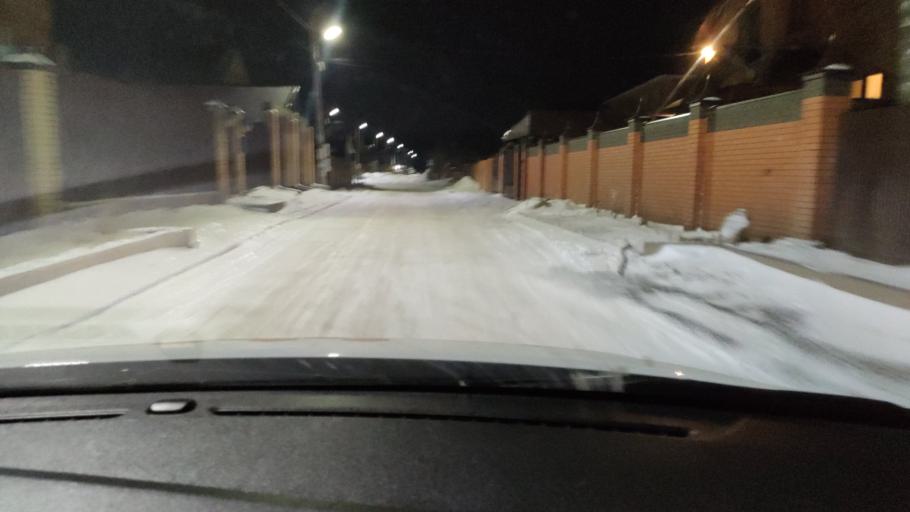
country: RU
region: Tatarstan
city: Vysokaya Gora
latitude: 55.8350
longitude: 49.2425
